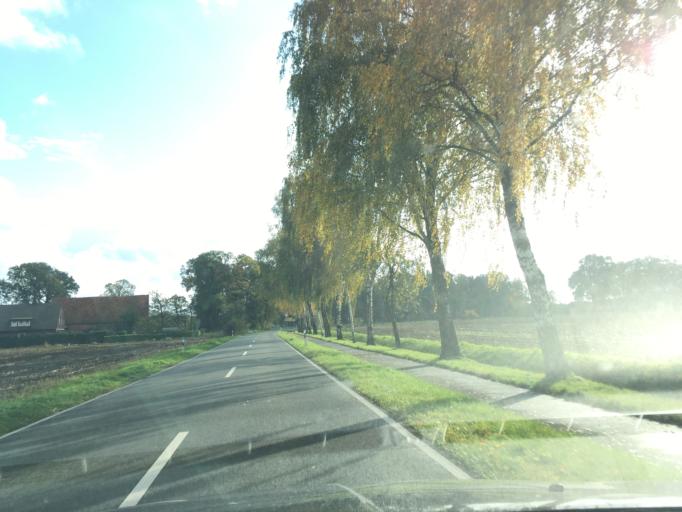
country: DE
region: North Rhine-Westphalia
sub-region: Regierungsbezirk Munster
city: Vreden
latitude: 52.0946
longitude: 6.8651
